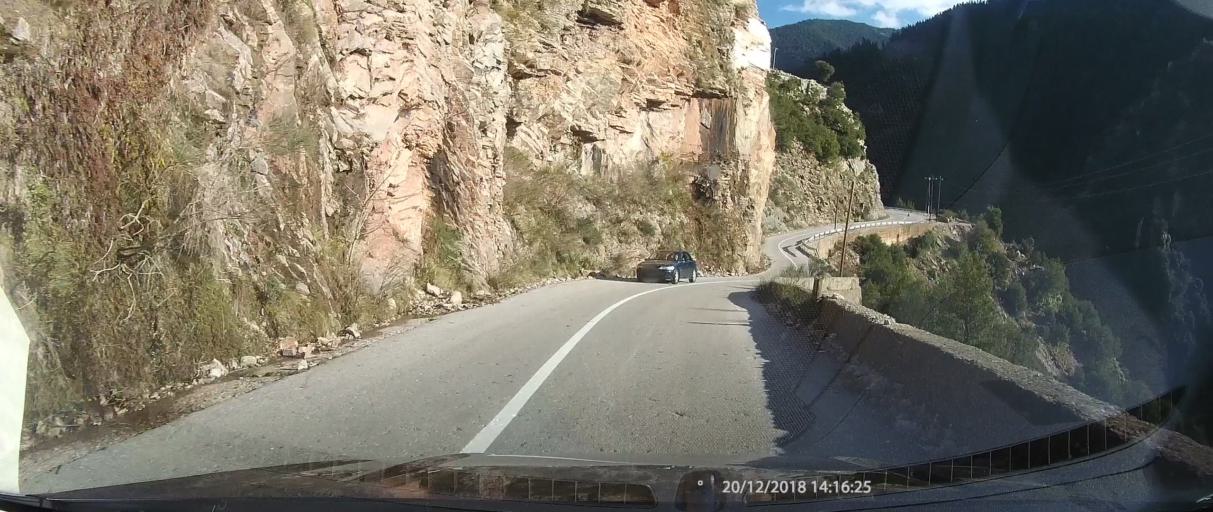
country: GR
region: West Greece
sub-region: Nomos Aitolias kai Akarnanias
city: Thermo
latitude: 38.7514
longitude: 21.6591
